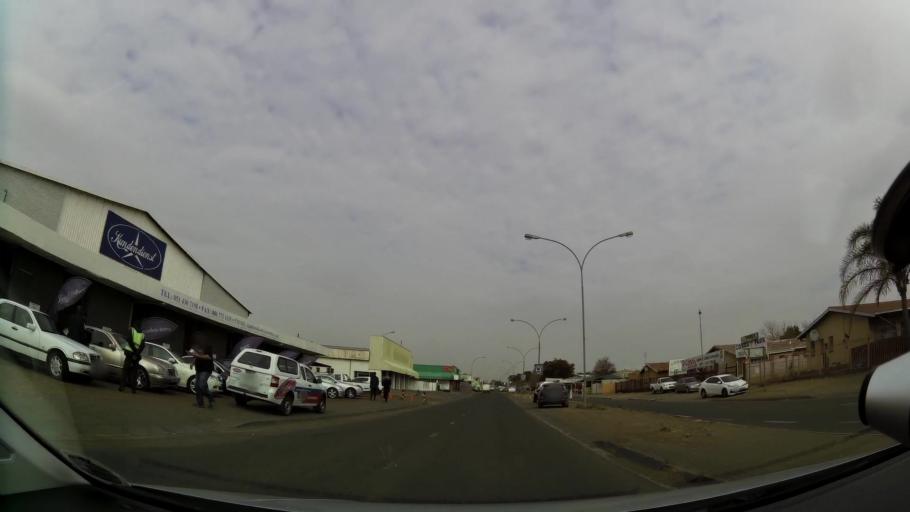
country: ZA
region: Orange Free State
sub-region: Mangaung Metropolitan Municipality
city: Bloemfontein
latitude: -29.1315
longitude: 26.2220
